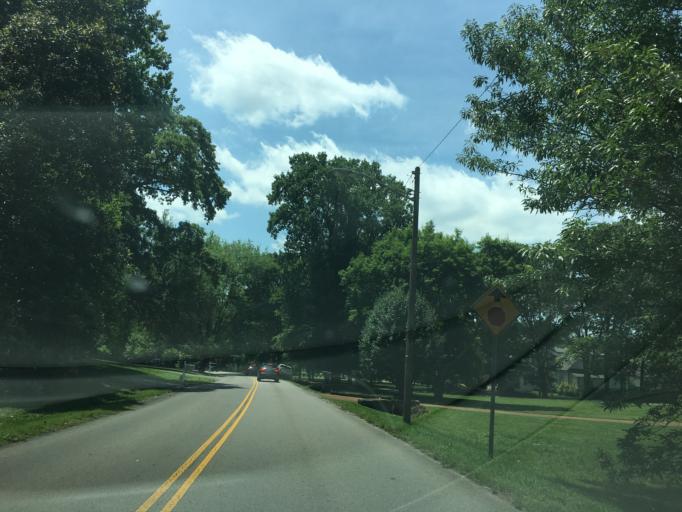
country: US
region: Tennessee
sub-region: Davidson County
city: Belle Meade
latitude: 36.1130
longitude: -86.8252
